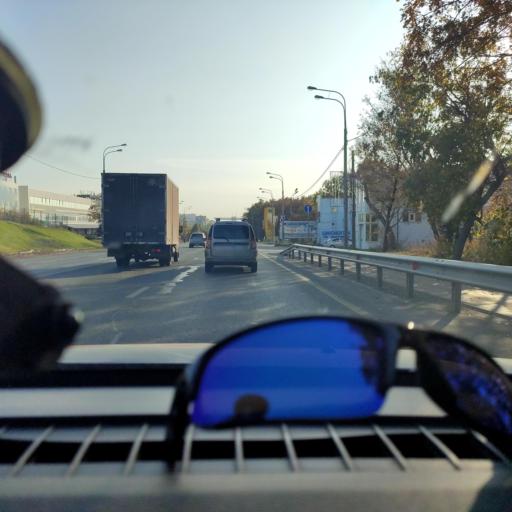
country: RU
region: Samara
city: Samara
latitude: 53.2751
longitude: 50.2267
